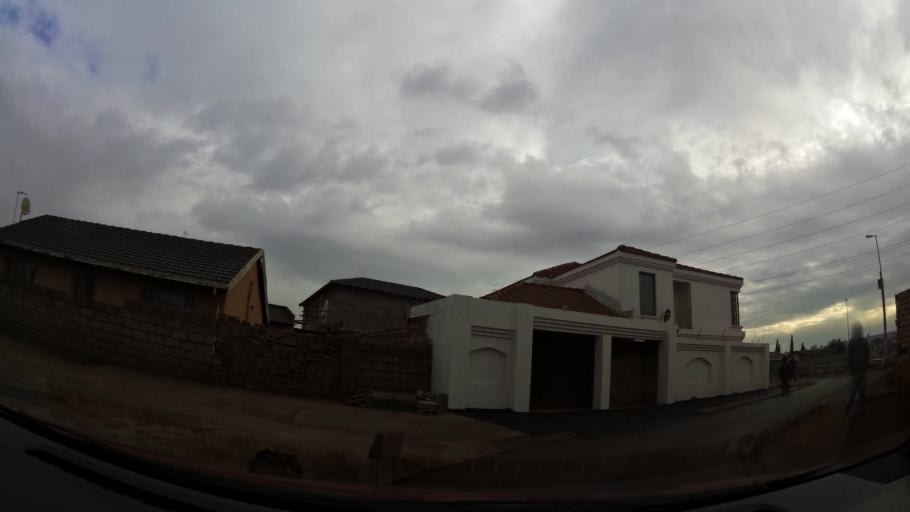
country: ZA
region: Gauteng
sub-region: City of Johannesburg Metropolitan Municipality
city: Soweto
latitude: -26.2839
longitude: 27.8481
